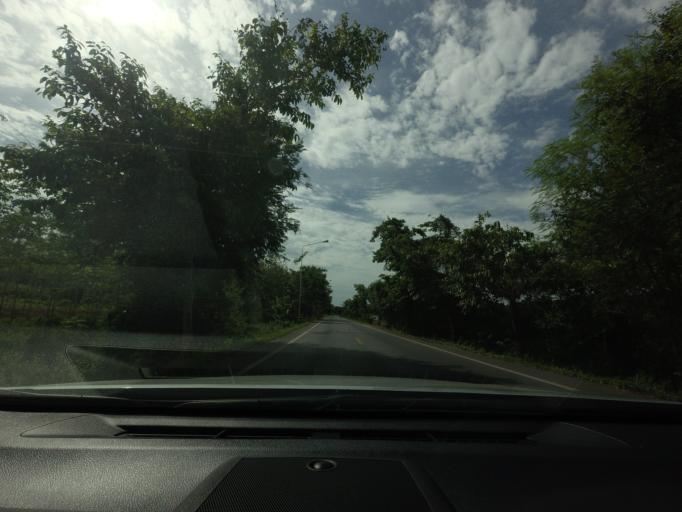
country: TH
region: Songkhla
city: Khlong Hoi Khong
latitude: 6.9040
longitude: 100.4140
